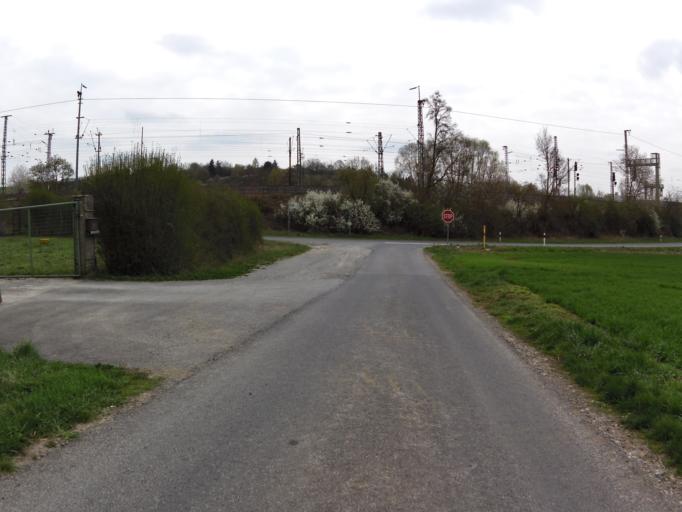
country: DE
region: Bavaria
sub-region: Regierungsbezirk Unterfranken
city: Rottendorf
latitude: 49.7991
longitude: 10.0306
